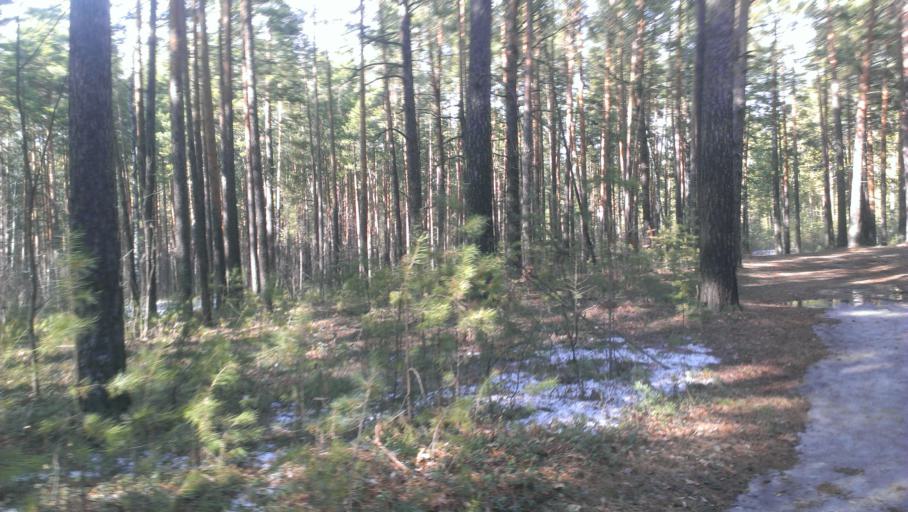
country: RU
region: Altai Krai
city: Yuzhnyy
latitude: 53.2828
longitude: 83.6992
